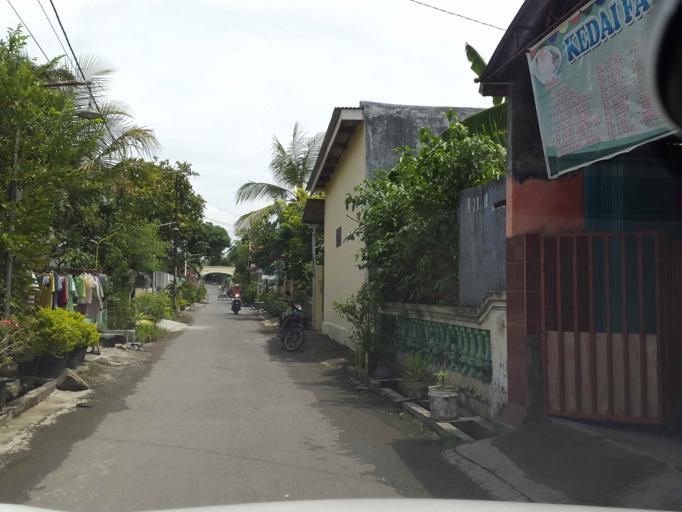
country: ID
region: East Java
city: Mojokerto
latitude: -7.4512
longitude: 112.4523
